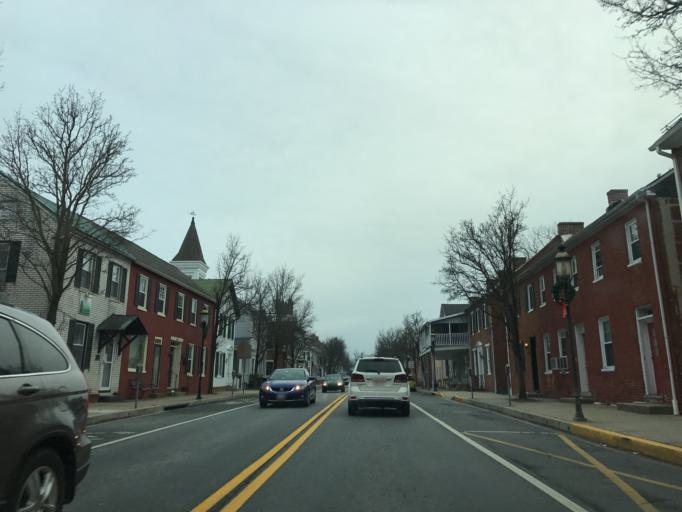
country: US
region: Maryland
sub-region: Frederick County
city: Emmitsburg
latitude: 39.7053
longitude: -77.3295
